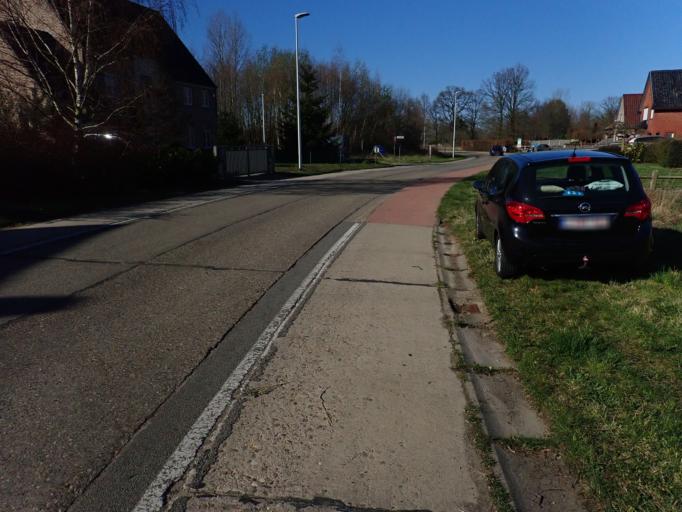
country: BE
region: Flanders
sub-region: Provincie Antwerpen
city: Laakdal
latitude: 51.0563
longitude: 4.9828
